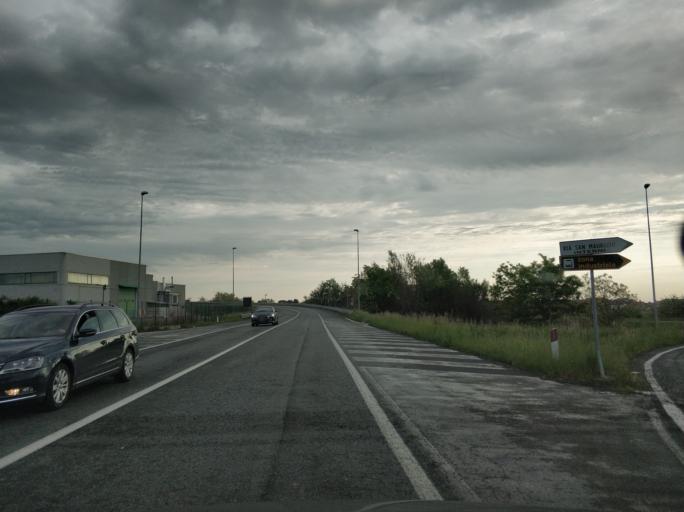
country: IT
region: Piedmont
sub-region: Provincia di Torino
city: San Maurizio
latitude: 45.2189
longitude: 7.6176
